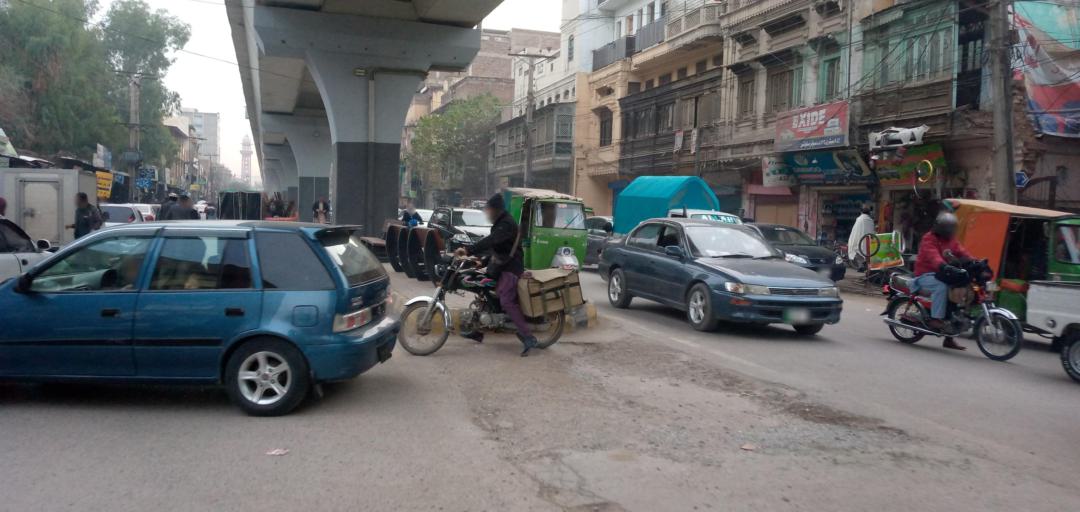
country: PK
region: Khyber Pakhtunkhwa
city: Peshawar
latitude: 33.9984
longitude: 71.5437
